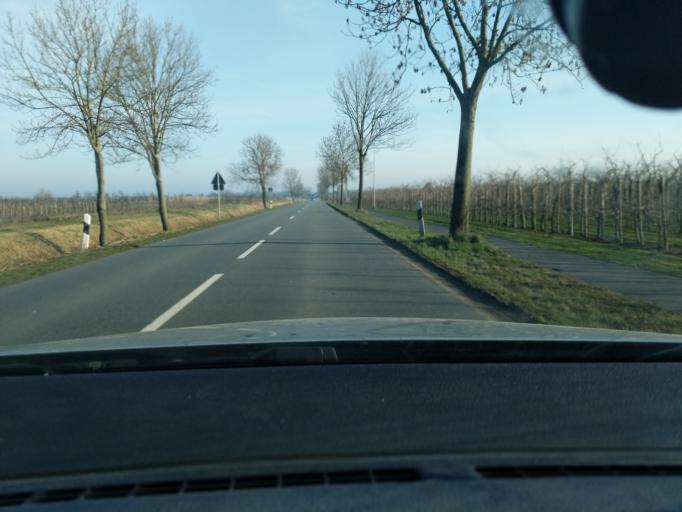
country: DE
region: Lower Saxony
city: Jork
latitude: 53.5430
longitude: 9.6591
